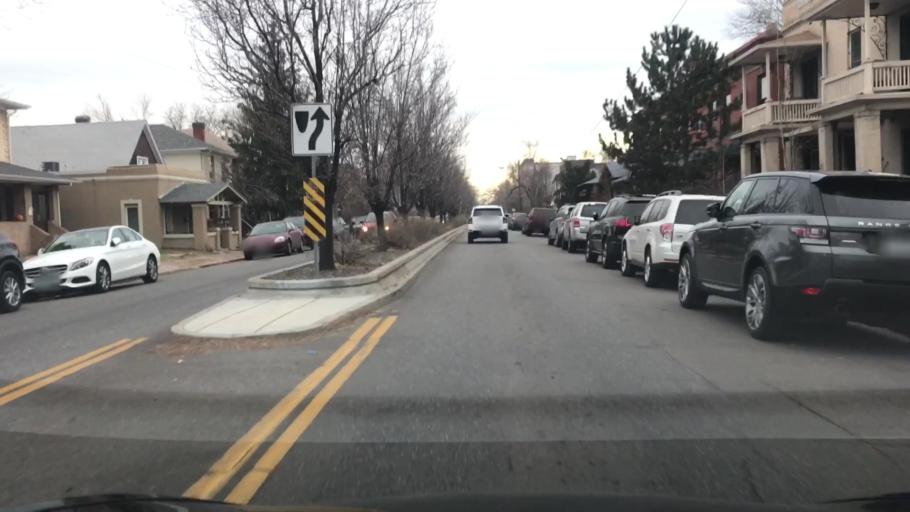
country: US
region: Colorado
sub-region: Denver County
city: Denver
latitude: 39.7179
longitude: -104.9826
